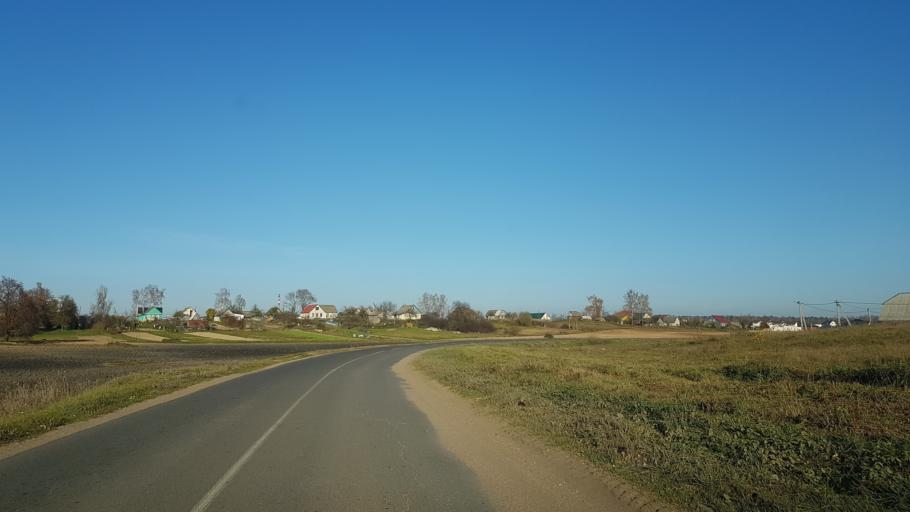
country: BY
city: Fanipol
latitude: 53.7234
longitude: 27.3143
